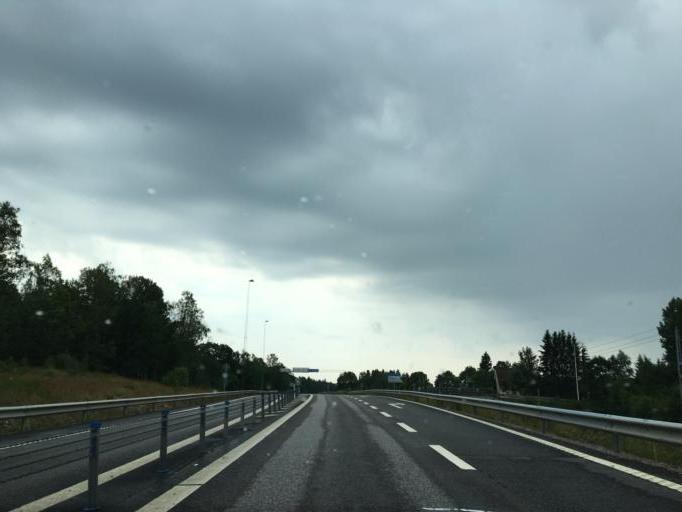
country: SE
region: OEstergoetland
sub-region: Norrkopings Kommun
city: Jursla
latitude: 58.7835
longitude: 16.1578
